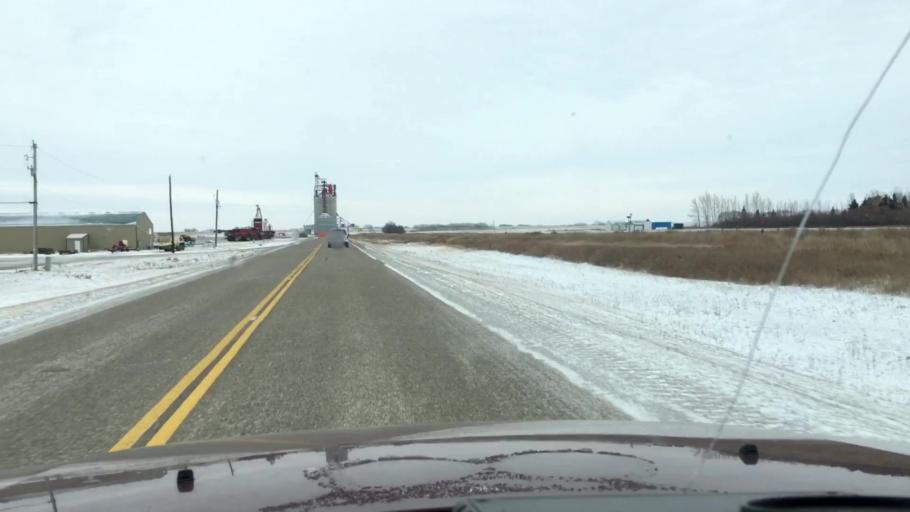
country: CA
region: Saskatchewan
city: Watrous
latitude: 51.2528
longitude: -105.9810
